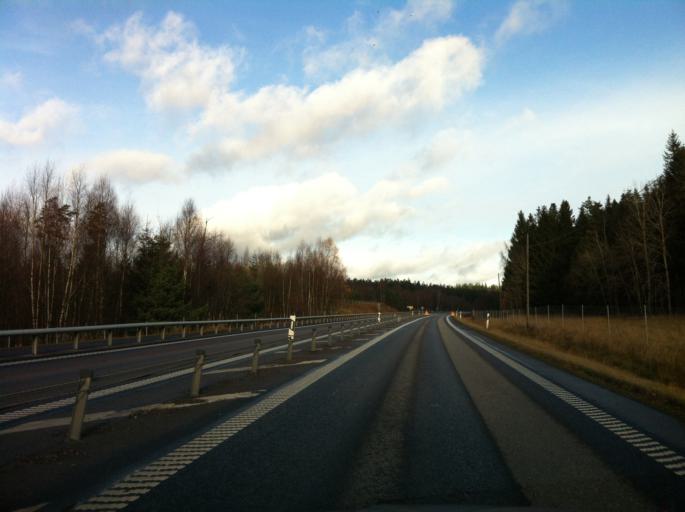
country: SE
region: Skane
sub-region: Osby Kommun
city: Osby
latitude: 56.3991
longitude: 14.0381
